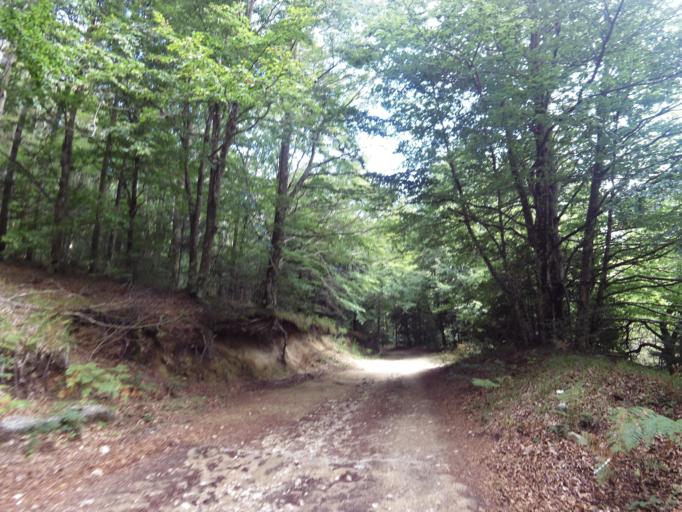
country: IT
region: Calabria
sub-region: Provincia di Vibo-Valentia
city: Mongiana
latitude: 38.5292
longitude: 16.3774
